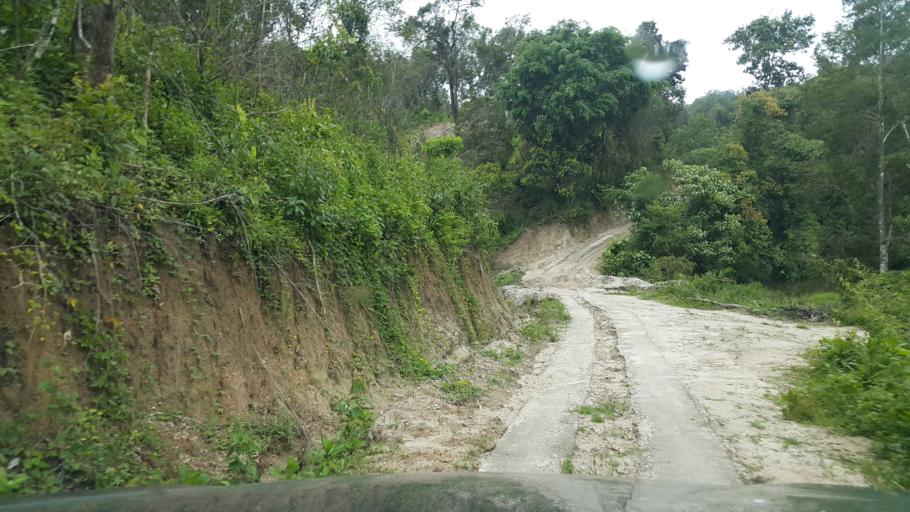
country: TH
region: Chiang Mai
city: Samoeng
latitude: 18.8092
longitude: 98.6244
